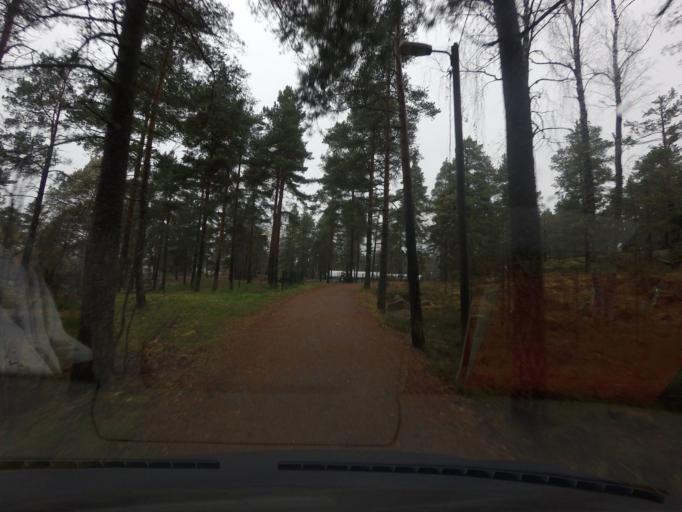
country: FI
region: Uusimaa
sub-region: Helsinki
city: Kauniainen
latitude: 60.2267
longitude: 24.7464
